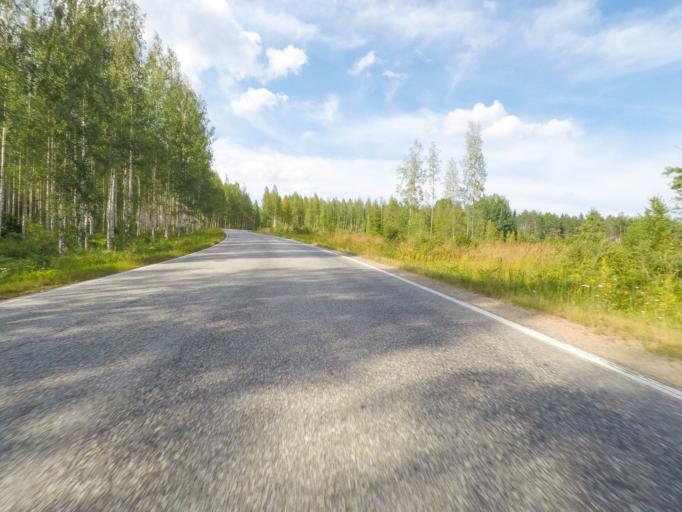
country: FI
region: Southern Savonia
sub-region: Mikkeli
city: Puumala
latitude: 61.7037
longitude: 28.2118
